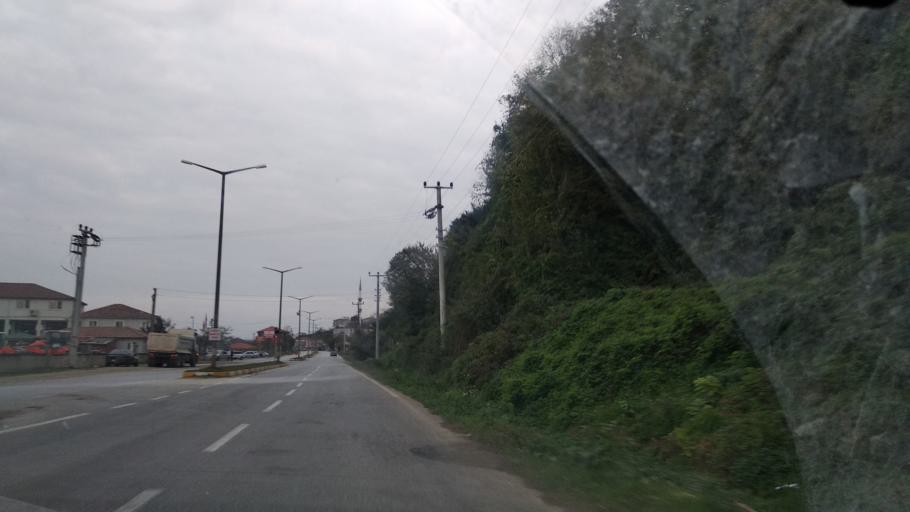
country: TR
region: Sakarya
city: Karasu
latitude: 41.0996
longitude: 30.6701
